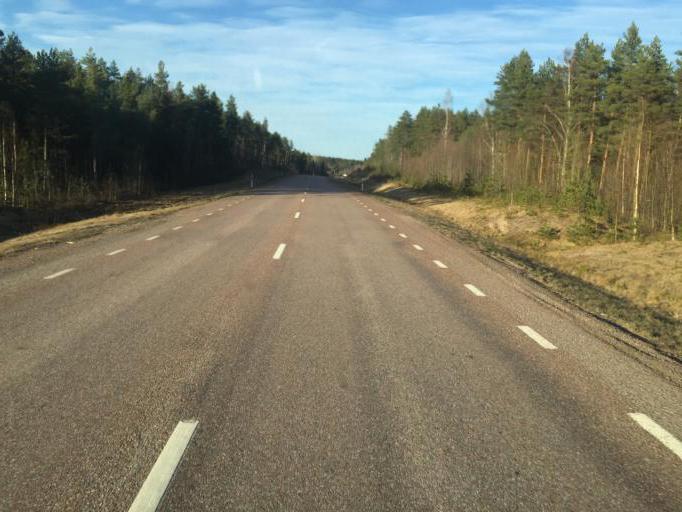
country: SE
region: Dalarna
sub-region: Gagnefs Kommun
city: Mockfjard
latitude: 60.5253
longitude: 15.0119
